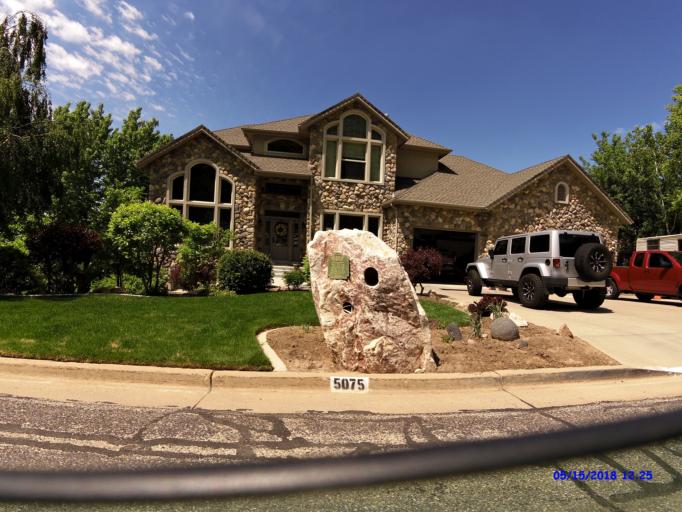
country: US
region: Utah
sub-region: Weber County
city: Uintah
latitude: 41.1709
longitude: -111.9240
